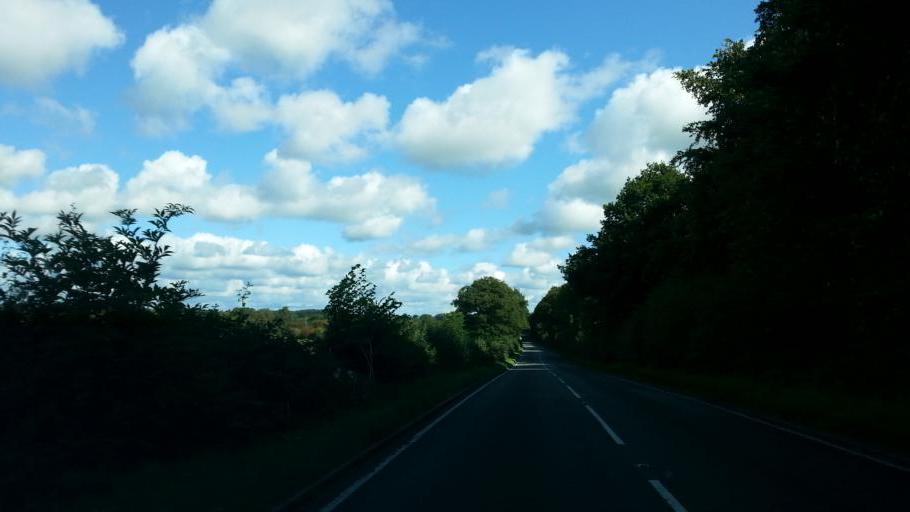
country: GB
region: England
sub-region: Staffordshire
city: Uttoxeter
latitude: 52.8513
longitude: -1.8996
